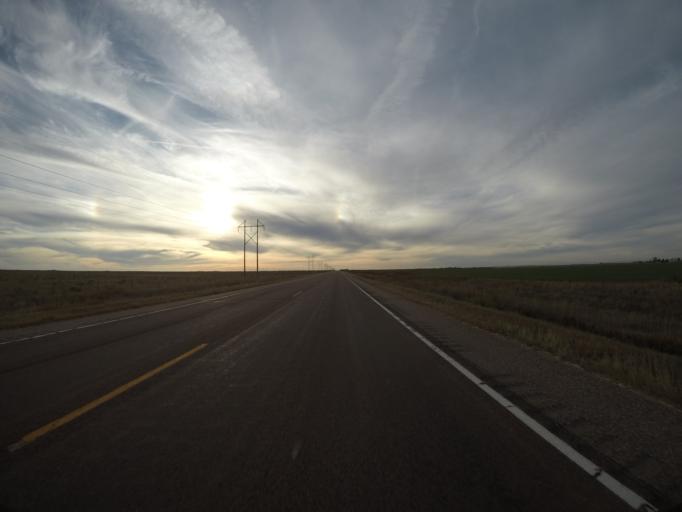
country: US
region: Colorado
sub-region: Yuma County
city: Yuma
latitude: 39.6559
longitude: -102.7192
